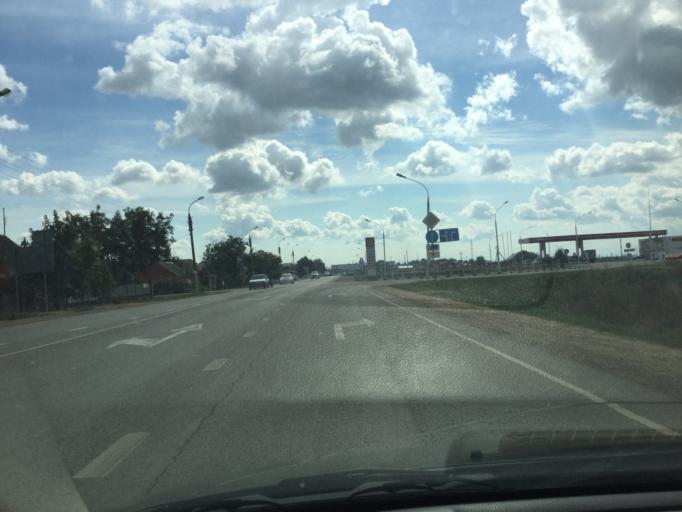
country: RU
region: Krasnodarskiy
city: Slavyansk-na-Kubani
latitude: 45.2483
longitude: 38.1007
